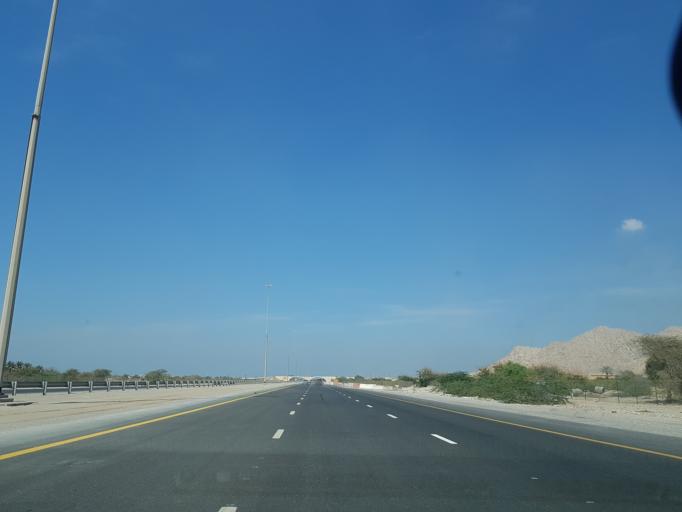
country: AE
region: Ra's al Khaymah
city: Ras al-Khaimah
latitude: 25.8121
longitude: 56.0286
